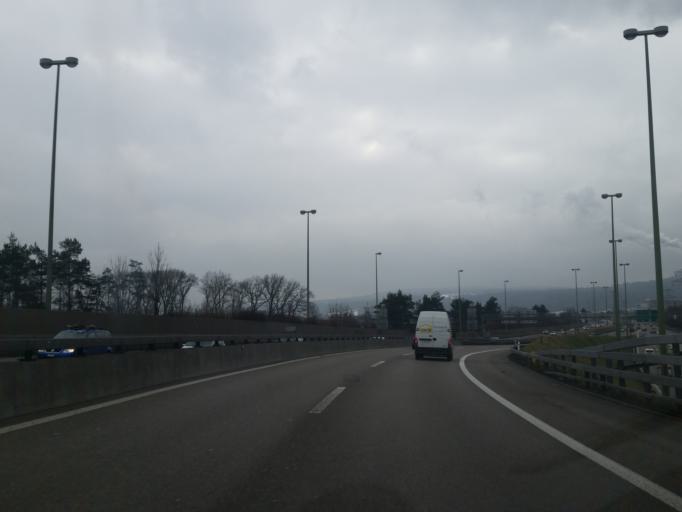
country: CH
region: Zurich
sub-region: Bezirk Buelach
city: Grossacker/Opfikon
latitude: 47.4226
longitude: 8.5739
